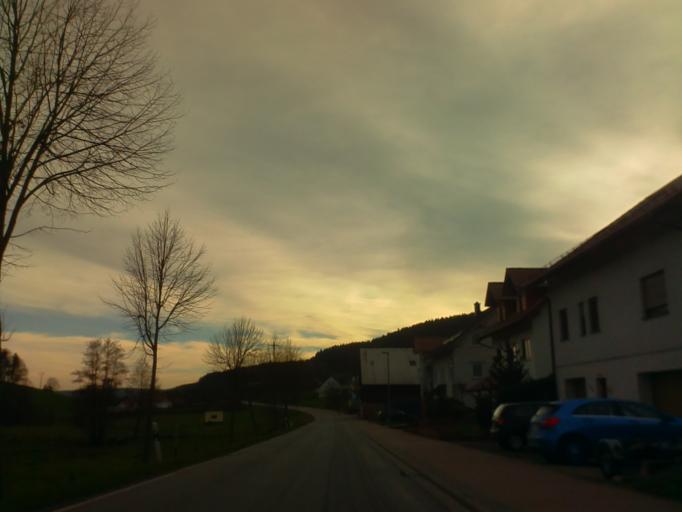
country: DE
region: Hesse
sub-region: Regierungsbezirk Darmstadt
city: Erbach
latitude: 49.6714
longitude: 8.9250
